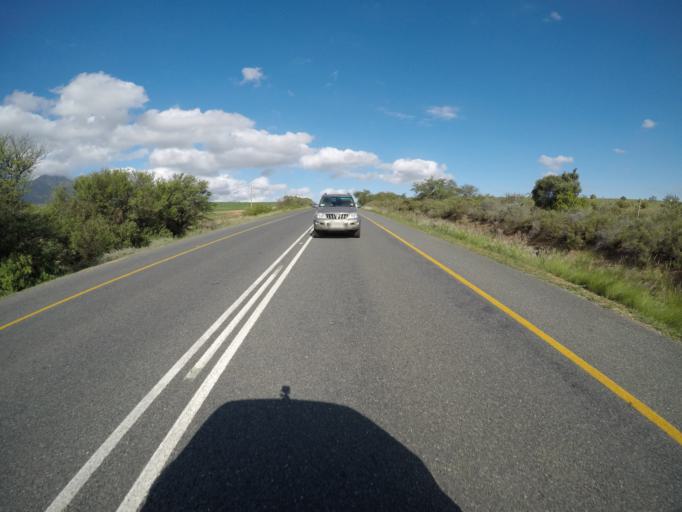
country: ZA
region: Western Cape
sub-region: Cape Winelands District Municipality
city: Ashton
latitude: -33.9530
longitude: 20.2304
